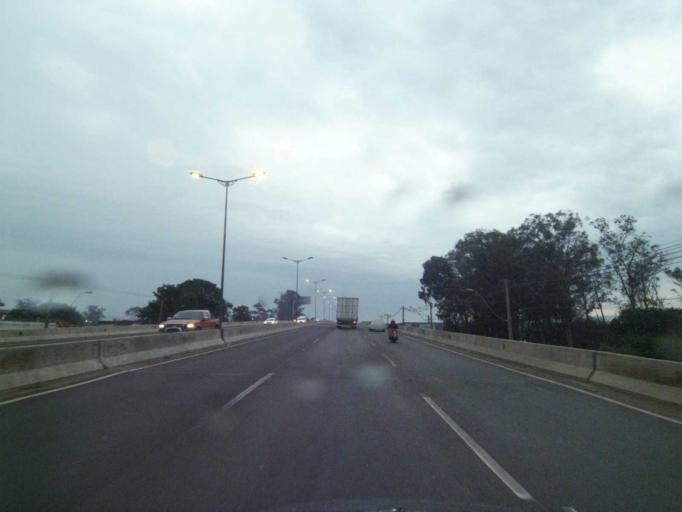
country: BR
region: Rio Grande do Sul
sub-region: Sapucaia Do Sul
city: Sapucaia
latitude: -29.8199
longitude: -51.1700
